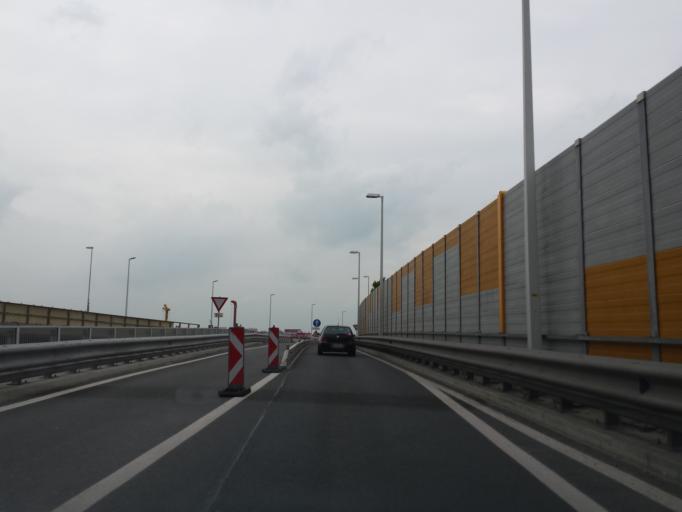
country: AT
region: Lower Austria
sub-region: Politischer Bezirk Modling
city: Vosendorf
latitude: 48.1488
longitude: 16.3344
